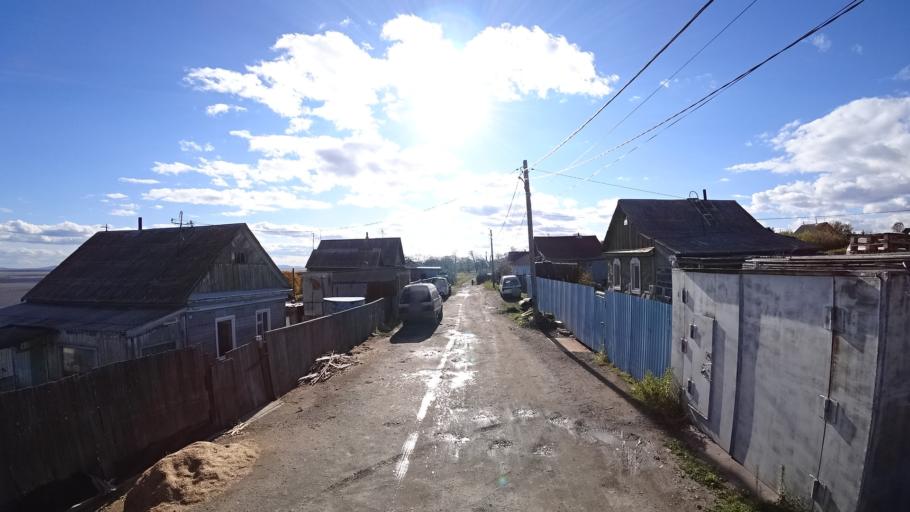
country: RU
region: Khabarovsk Krai
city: Amursk
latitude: 50.2318
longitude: 136.9189
